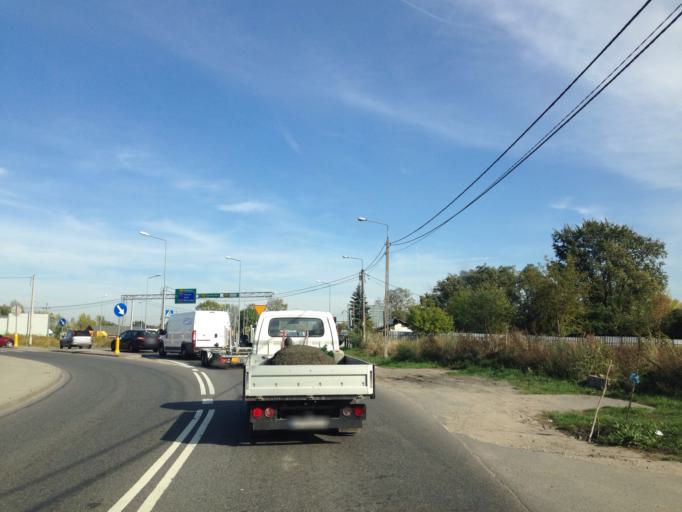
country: PL
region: Masovian Voivodeship
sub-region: Powiat warszawski zachodni
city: Ozarow Mazowiecki
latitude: 52.1822
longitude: 20.7804
